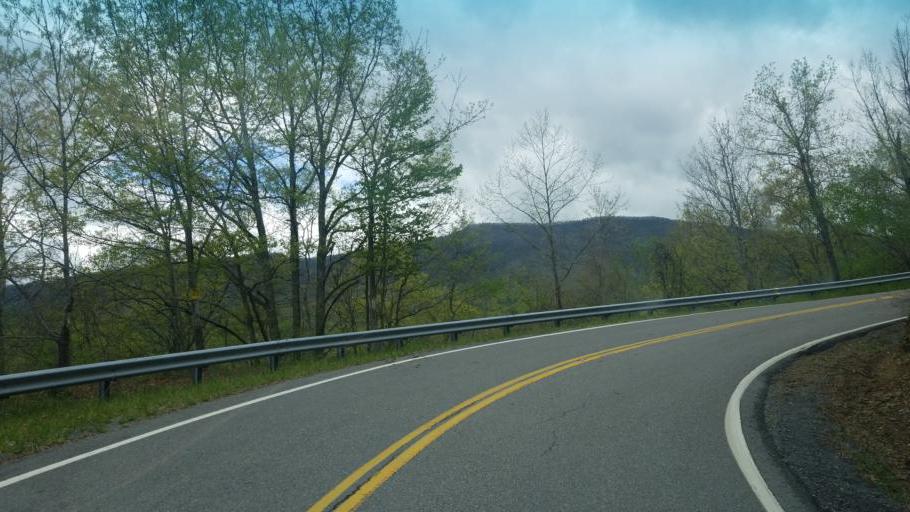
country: US
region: Virginia
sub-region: Tazewell County
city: Tazewell
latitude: 37.0122
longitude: -81.5219
